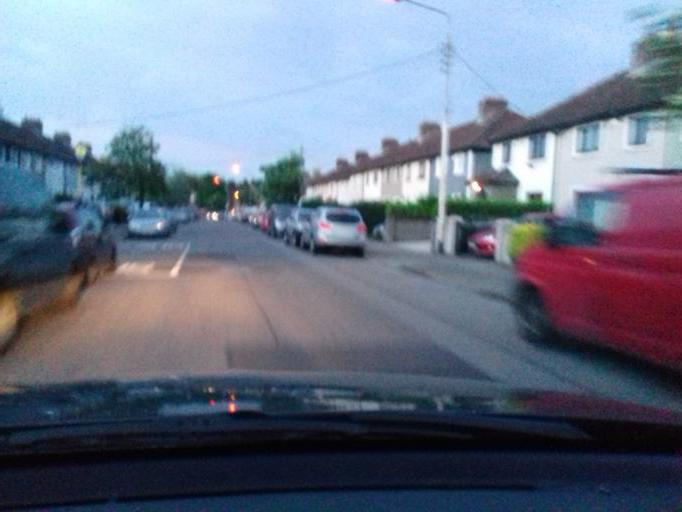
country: IE
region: Leinster
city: Crumlin
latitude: 53.3302
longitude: -6.3226
